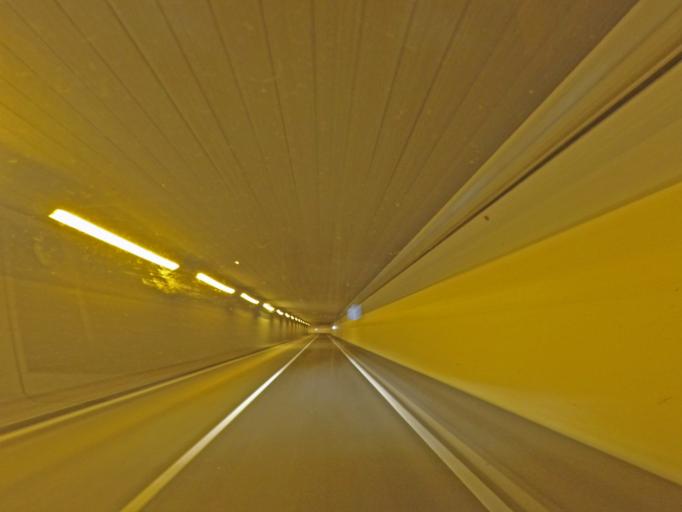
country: IT
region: Piedmont
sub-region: Provincia Verbano-Cusio-Ossola
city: Formazza
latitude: 46.5182
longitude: 8.3280
